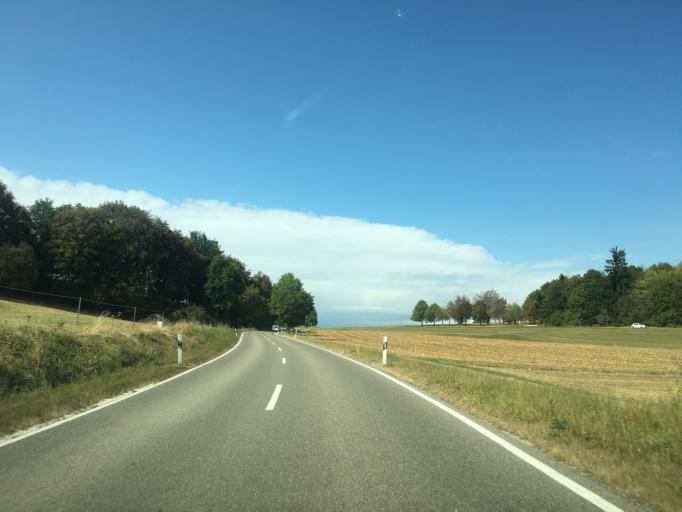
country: DE
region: Baden-Wuerttemberg
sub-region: Tuebingen Region
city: Trochtelfingen
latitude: 48.3790
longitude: 9.1960
